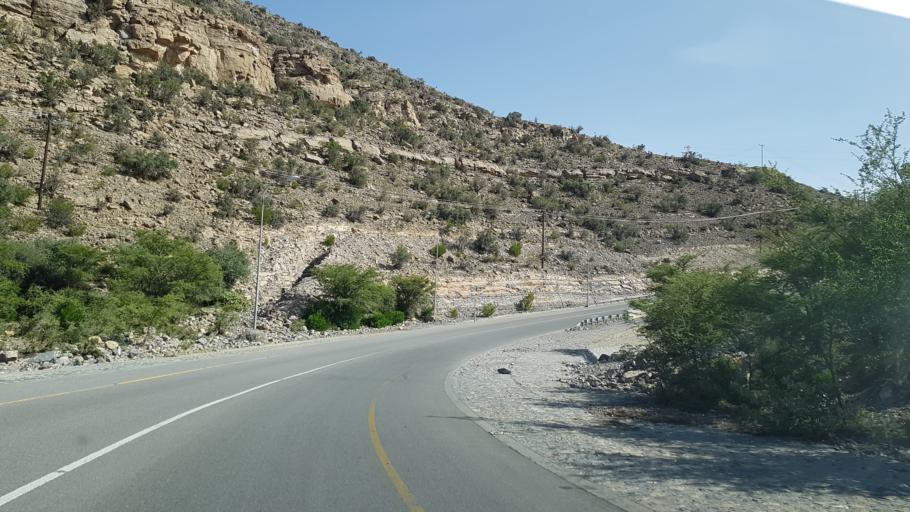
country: OM
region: Muhafazat ad Dakhiliyah
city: Izki
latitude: 23.0738
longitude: 57.7132
